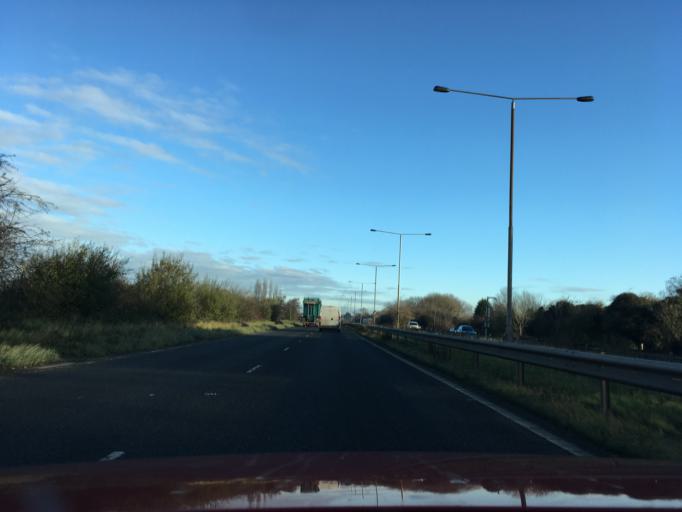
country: GB
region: England
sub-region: Derbyshire
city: Etwall
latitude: 52.8435
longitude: -1.5977
